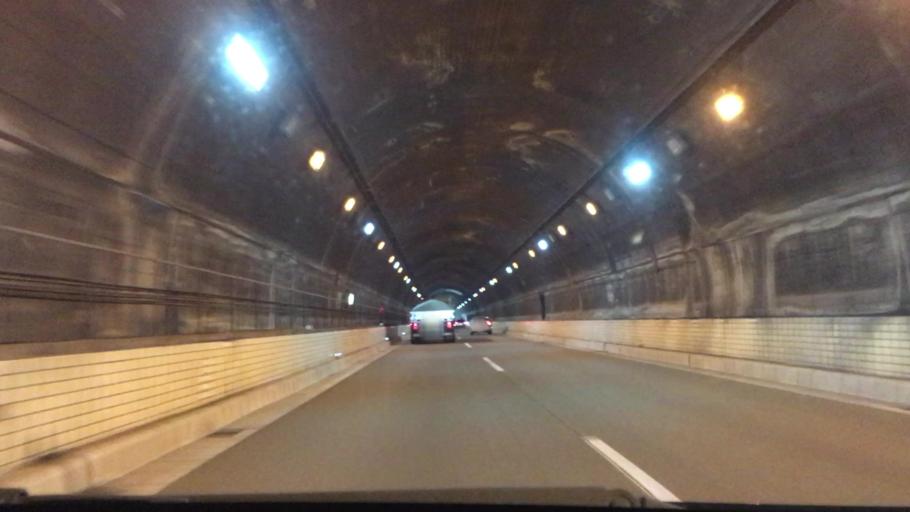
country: JP
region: Yamaguchi
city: Shimonoseki
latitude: 33.9570
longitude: 130.9682
